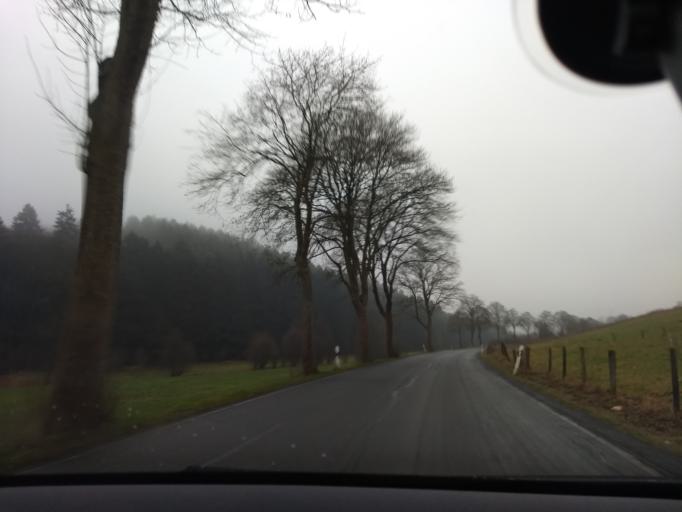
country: DE
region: North Rhine-Westphalia
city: Eslohe
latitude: 51.2501
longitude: 8.1464
